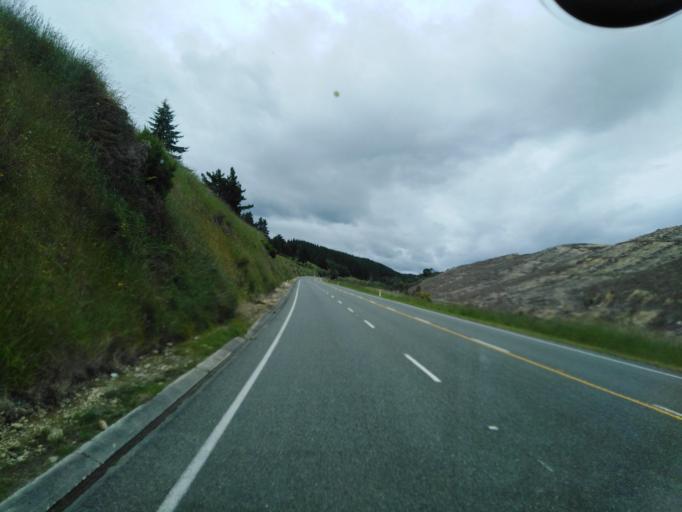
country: NZ
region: Tasman
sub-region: Tasman District
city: Wakefield
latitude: -41.4673
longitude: 172.9448
